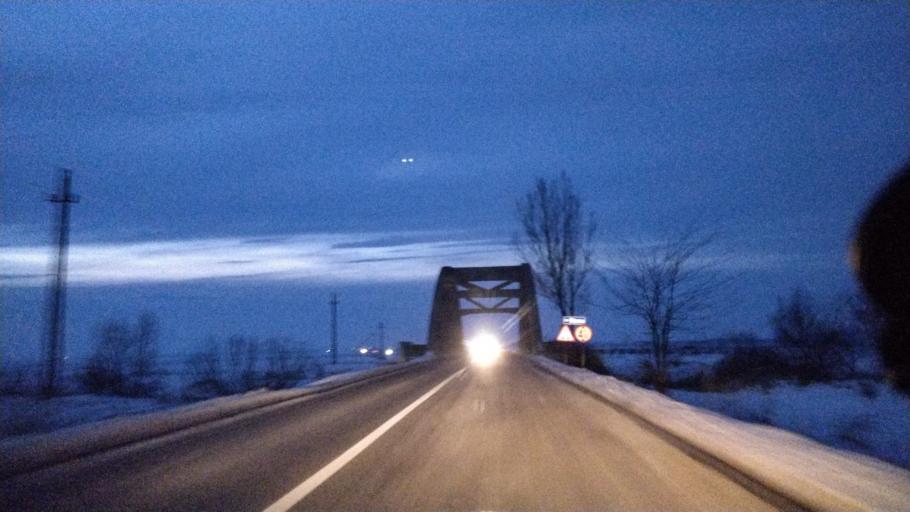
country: RO
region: Vrancea
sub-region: Comuna Rastoaca
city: Rastoaca
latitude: 45.6491
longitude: 27.3180
